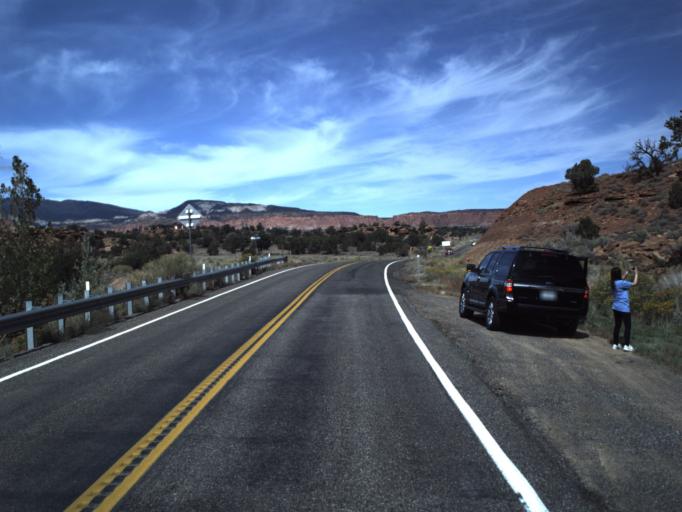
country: US
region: Utah
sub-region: Wayne County
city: Loa
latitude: 38.2843
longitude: -111.3958
